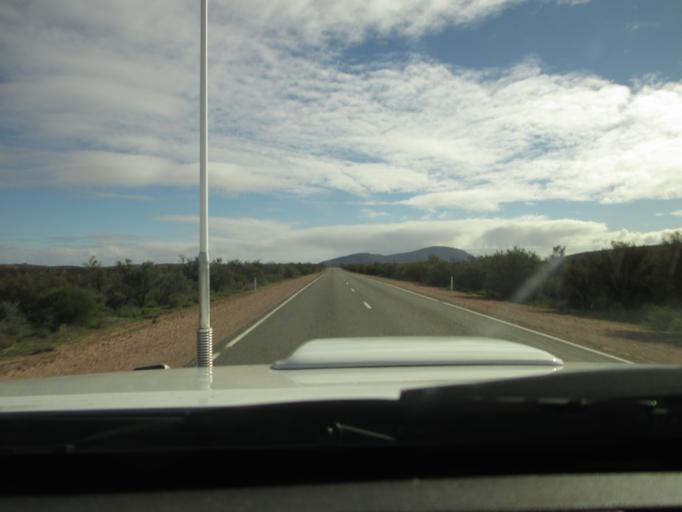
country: AU
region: South Australia
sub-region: Flinders Ranges
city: Quorn
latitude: -31.8465
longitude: 138.3943
